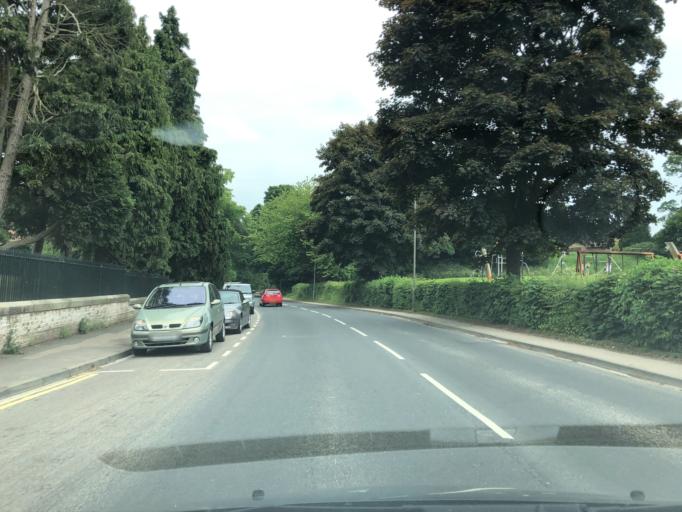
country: GB
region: England
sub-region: North Yorkshire
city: Boroughbridge
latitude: 54.0903
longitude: -1.3975
